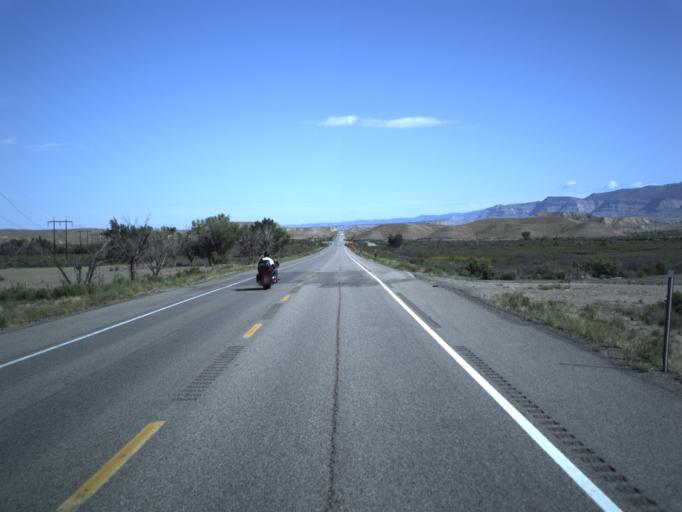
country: US
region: Utah
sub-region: Carbon County
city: East Carbon City
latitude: 39.2594
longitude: -110.3412
